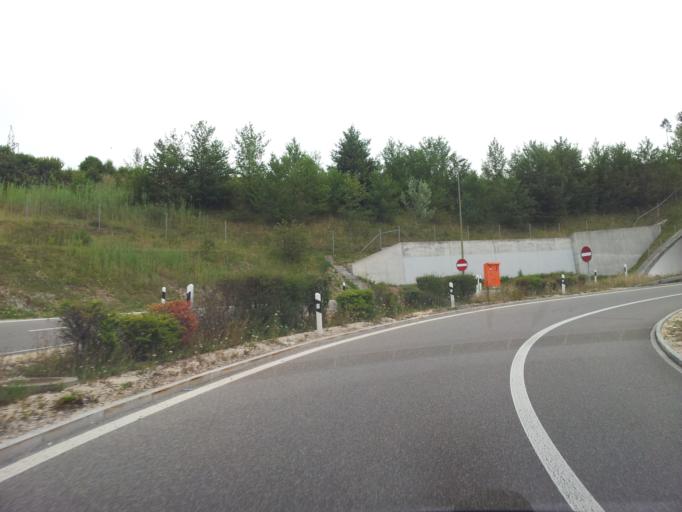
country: CH
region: Zurich
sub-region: Bezirk Dietikon
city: Birmensdorf
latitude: 47.3479
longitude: 8.4290
